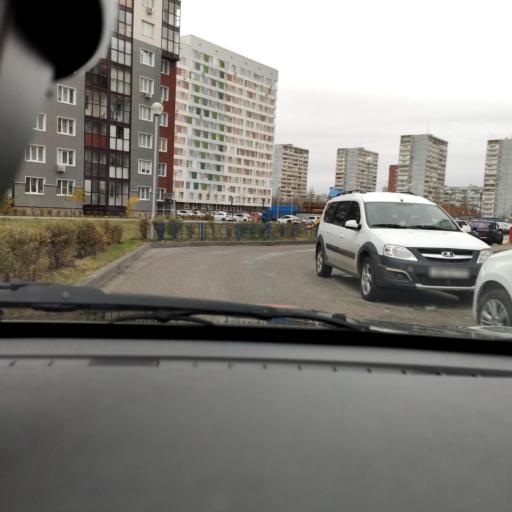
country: RU
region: Samara
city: Tol'yatti
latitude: 53.5288
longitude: 49.3422
